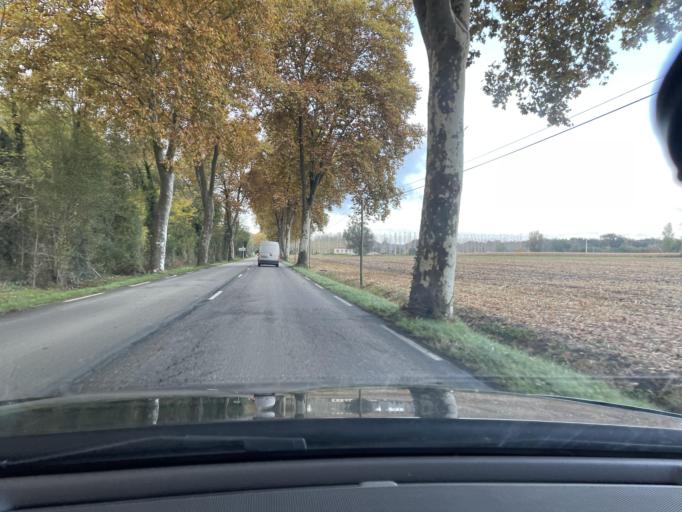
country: FR
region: Aquitaine
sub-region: Departement du Lot-et-Garonne
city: Casteljaloux
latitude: 44.3752
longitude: 0.1058
